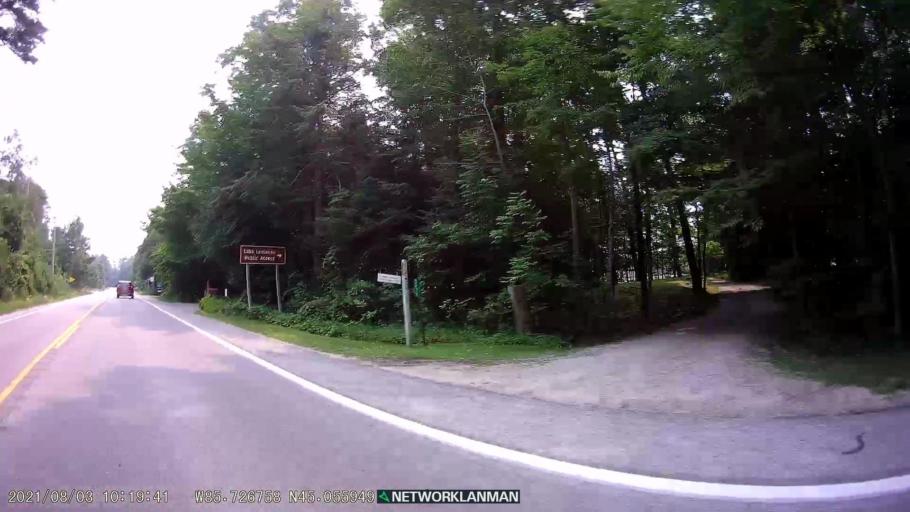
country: US
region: Michigan
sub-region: Leelanau County
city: Leland
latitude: 45.0558
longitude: -85.7265
